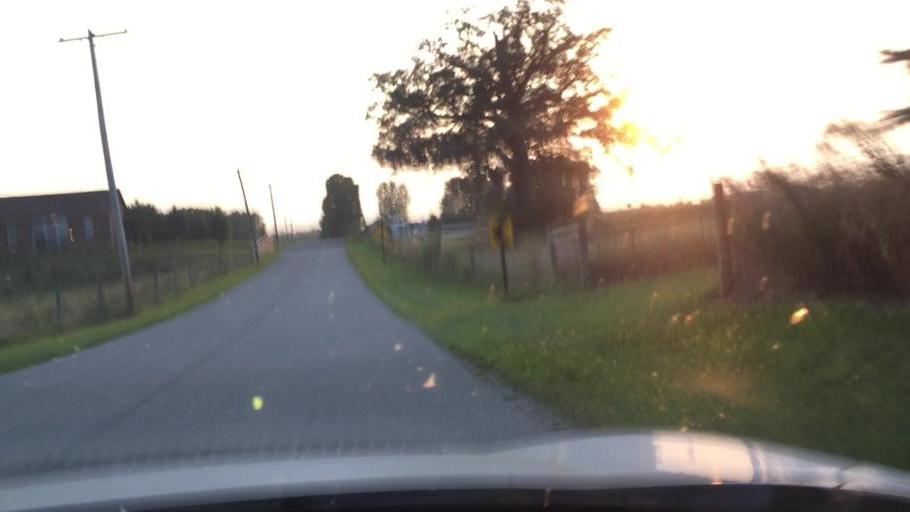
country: US
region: Ohio
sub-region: Madison County
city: Choctaw Lake
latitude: 39.9490
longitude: -83.5687
